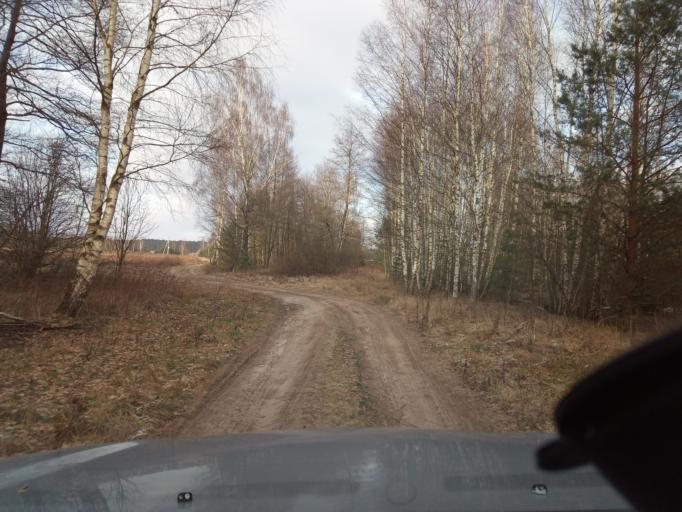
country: LT
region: Alytaus apskritis
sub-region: Alytaus rajonas
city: Daugai
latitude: 54.1118
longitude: 24.2396
